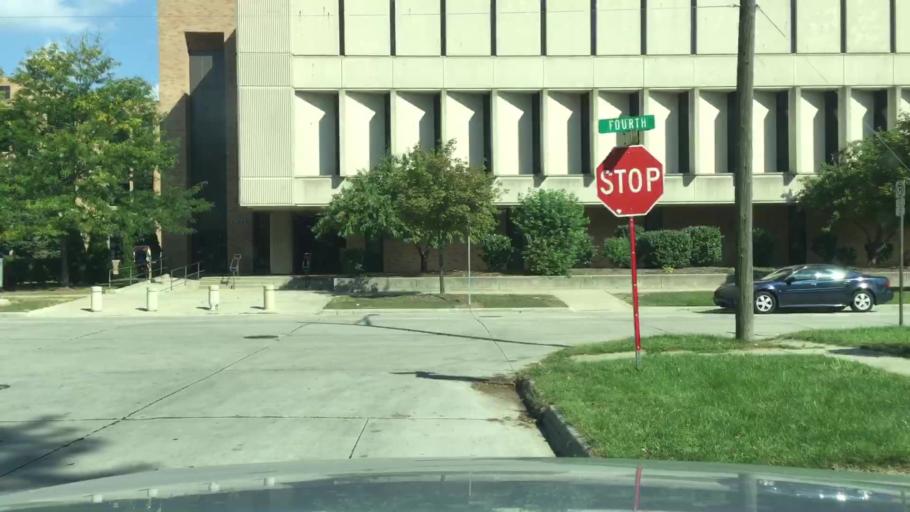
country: US
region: Michigan
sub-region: Wayne County
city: Wayne
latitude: 42.2876
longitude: -83.3783
